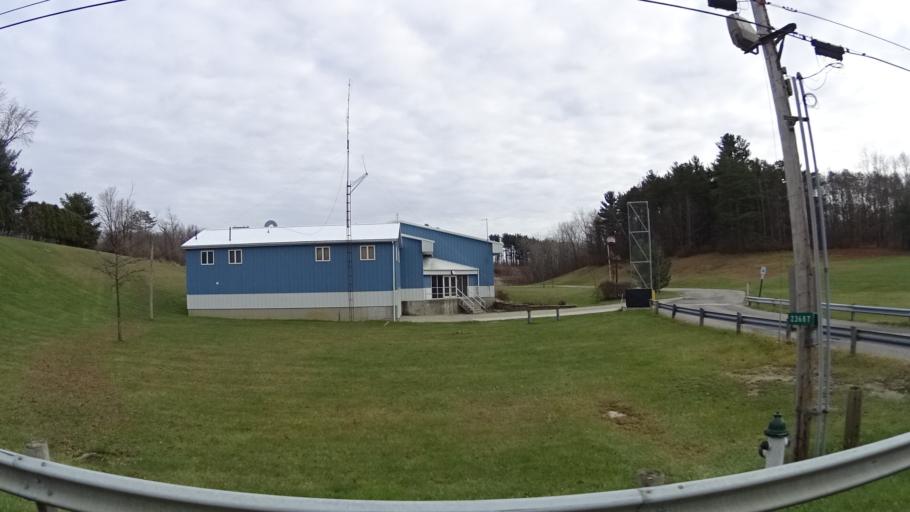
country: US
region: Ohio
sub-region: Lorain County
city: Wellington
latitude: 41.1513
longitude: -82.2435
